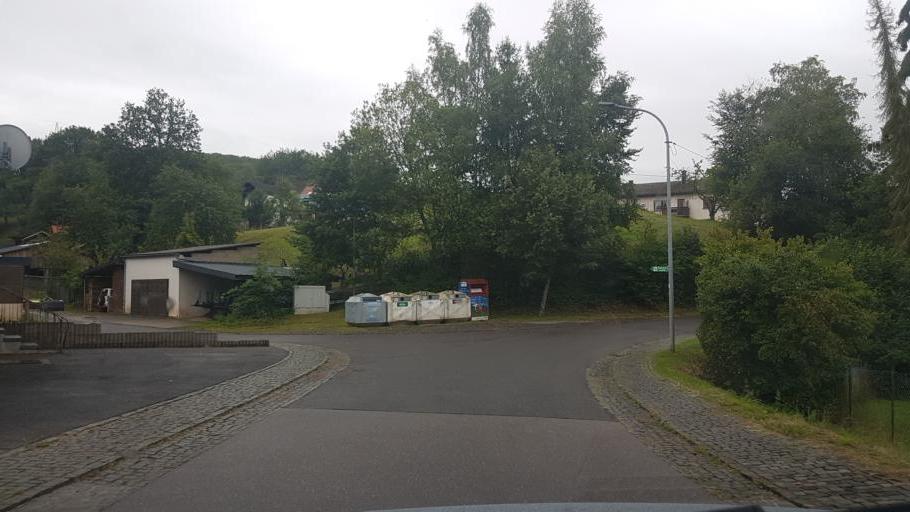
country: DE
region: Saarland
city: Wadern
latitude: 49.5514
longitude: 6.9210
